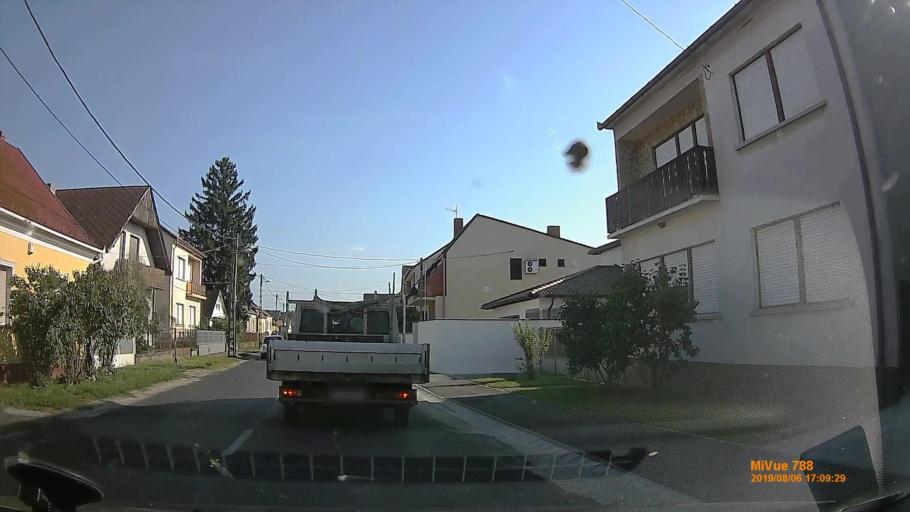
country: HU
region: Zala
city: Nagykanizsa
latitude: 46.4533
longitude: 16.9563
